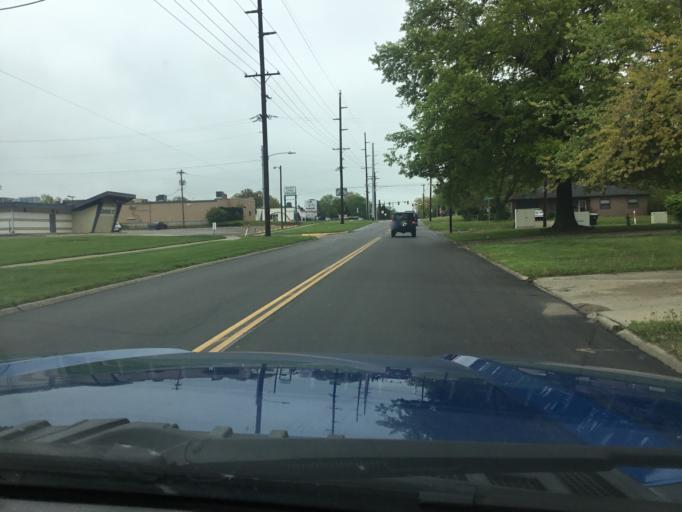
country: US
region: Kansas
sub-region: Shawnee County
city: Topeka
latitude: 39.0365
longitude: -95.7463
